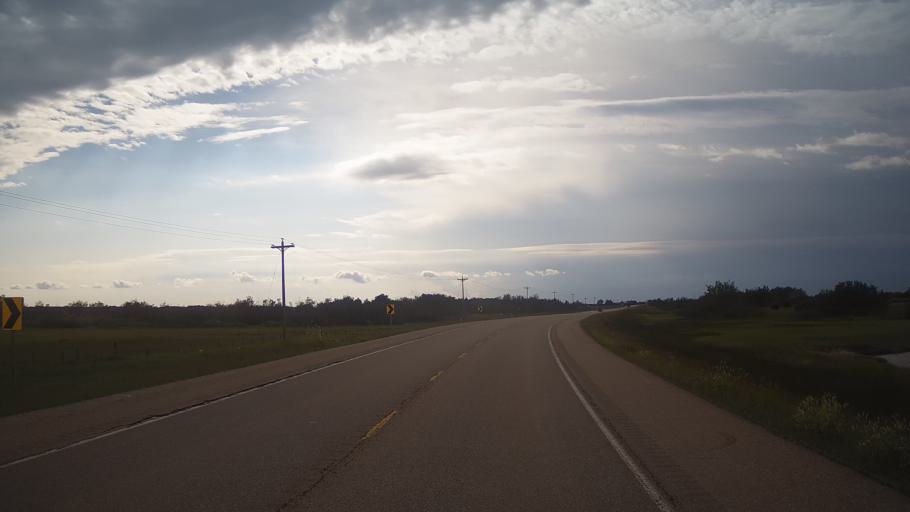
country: CA
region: Alberta
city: Viking
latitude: 53.1318
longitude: -111.9112
